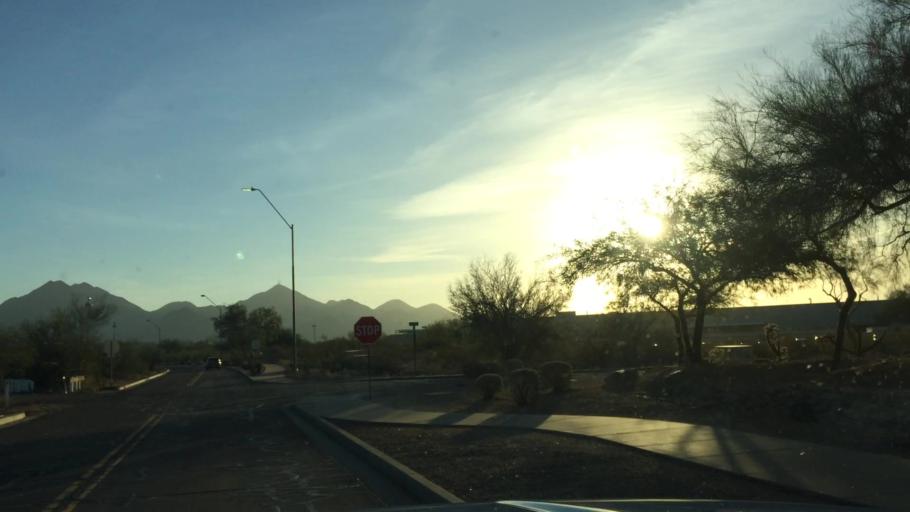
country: US
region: Arizona
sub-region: Maricopa County
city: Paradise Valley
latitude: 33.6494
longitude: -111.9041
